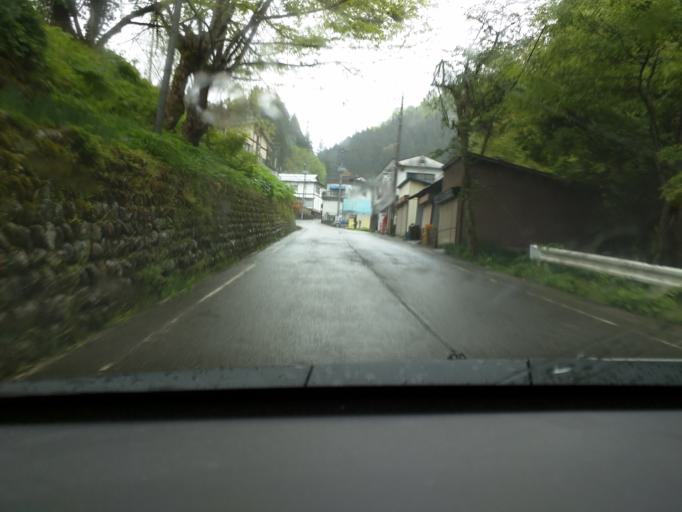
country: JP
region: Fukushima
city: Kitakata
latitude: 37.7308
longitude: 139.8859
